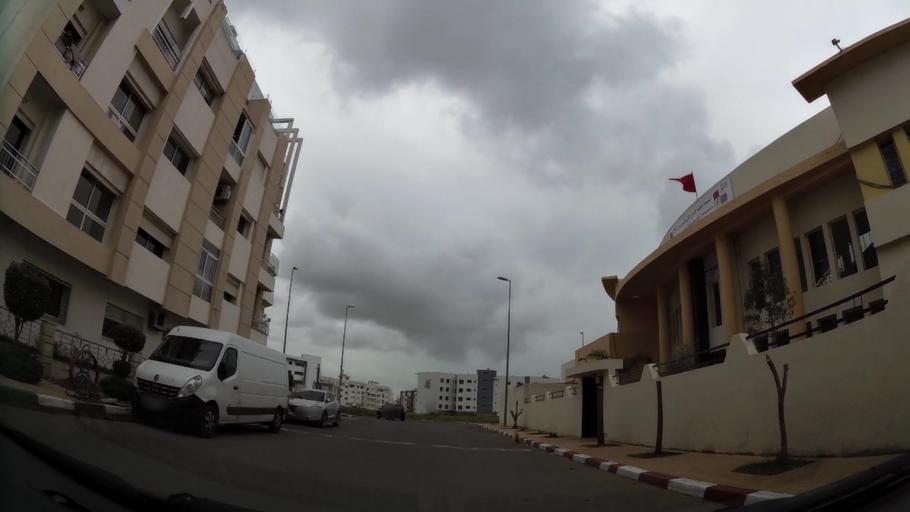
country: MA
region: Grand Casablanca
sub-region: Casablanca
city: Casablanca
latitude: 33.5298
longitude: -7.6119
